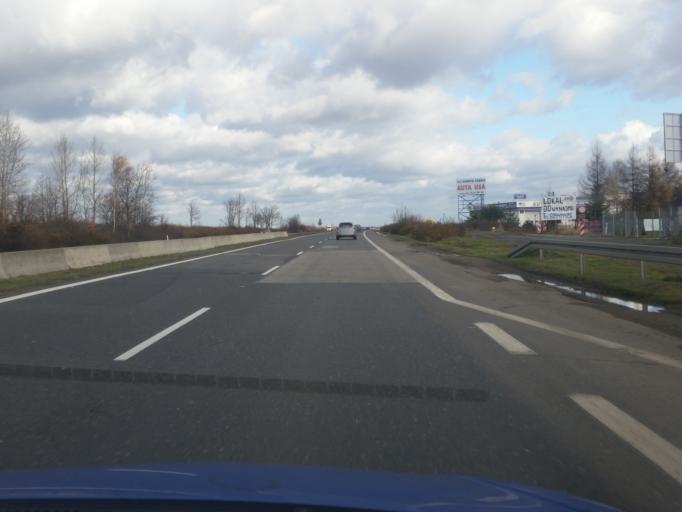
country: PL
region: Silesian Voivodeship
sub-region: Powiat czestochowski
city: Redziny
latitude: 50.8729
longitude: 19.1589
